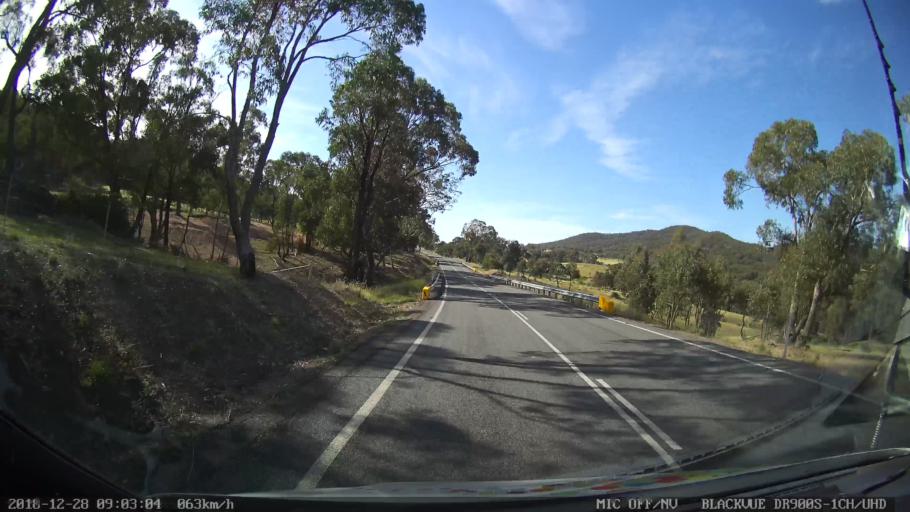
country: AU
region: New South Wales
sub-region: Upper Lachlan Shire
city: Crookwell
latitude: -34.1599
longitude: 149.3355
